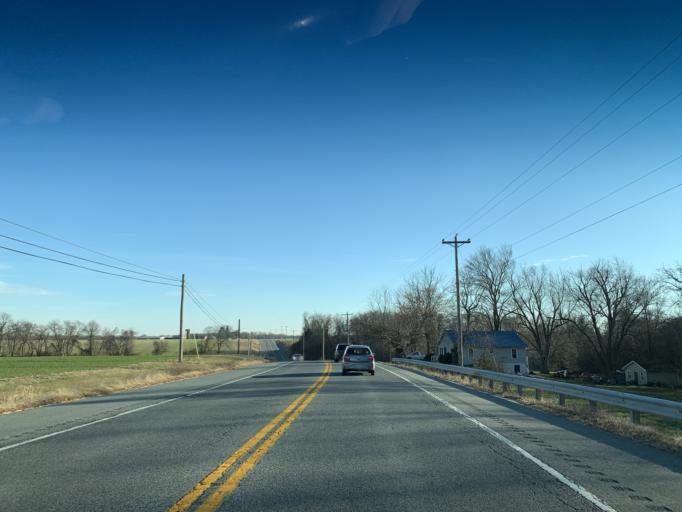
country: US
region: Delaware
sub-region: New Castle County
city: Middletown
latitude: 39.4463
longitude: -75.8687
